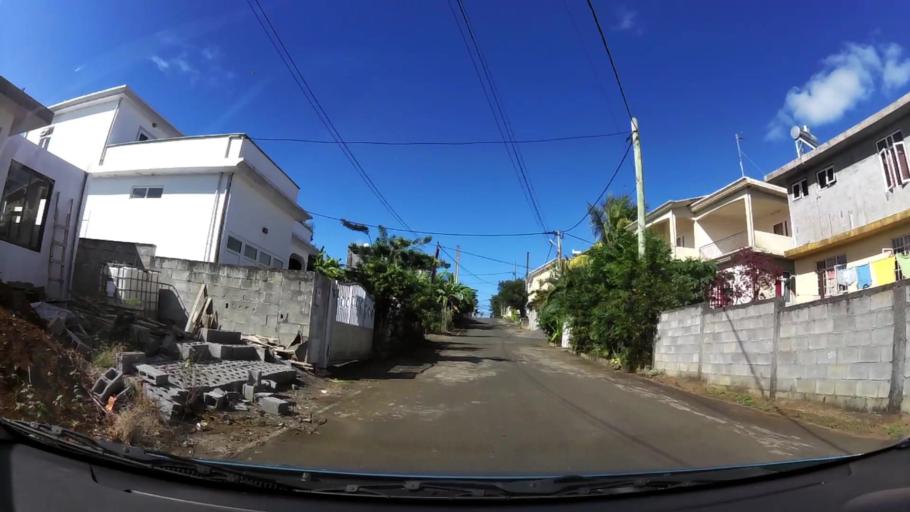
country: MU
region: Grand Port
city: Mahebourg
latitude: -20.4062
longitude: 57.6987
